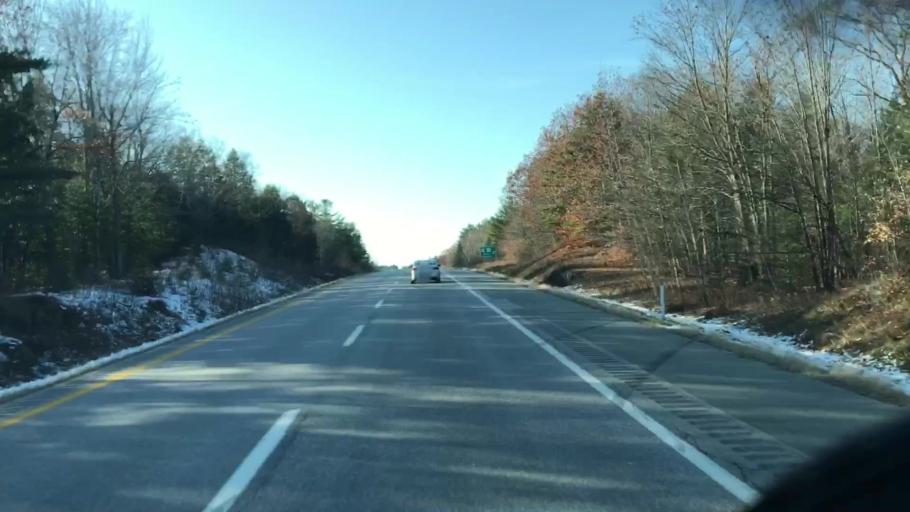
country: US
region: Maine
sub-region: Penobscot County
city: Etna
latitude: 44.7835
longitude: -69.0948
